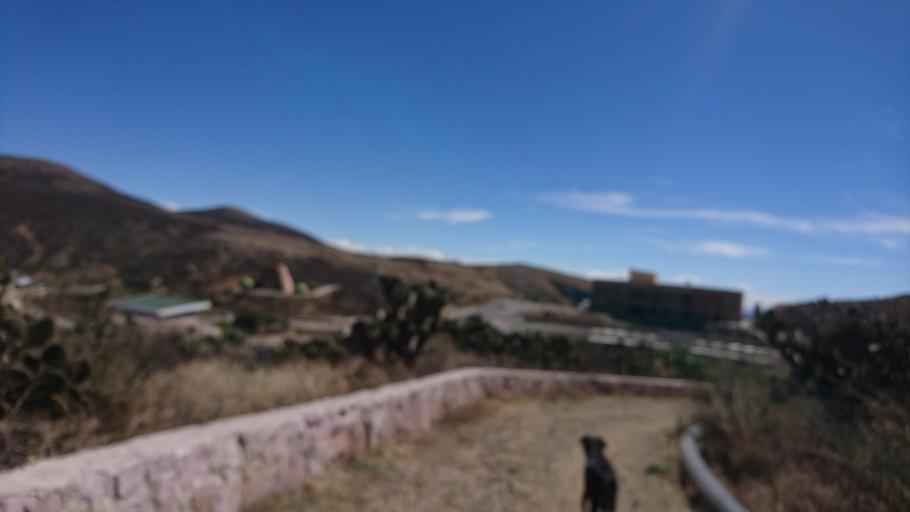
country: MX
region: Zacatecas
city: Zacatecas
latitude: 22.7815
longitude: -102.5461
